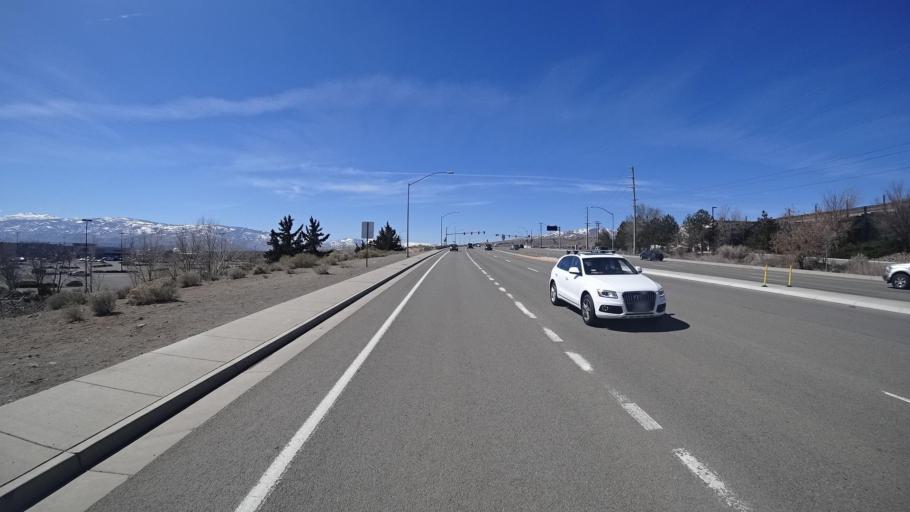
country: US
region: Nevada
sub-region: Washoe County
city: Sparks
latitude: 39.5565
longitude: -119.7844
